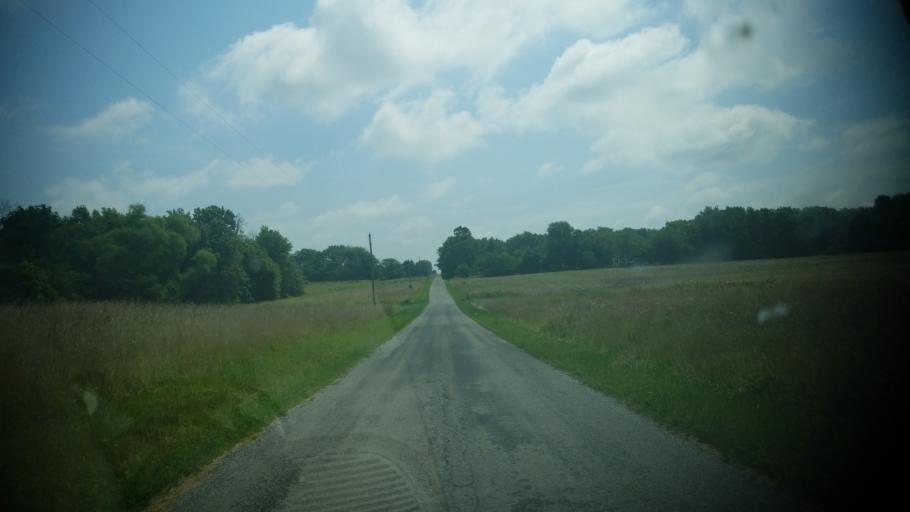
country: US
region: Illinois
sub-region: Wayne County
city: Fairfield
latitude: 38.5300
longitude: -88.4005
